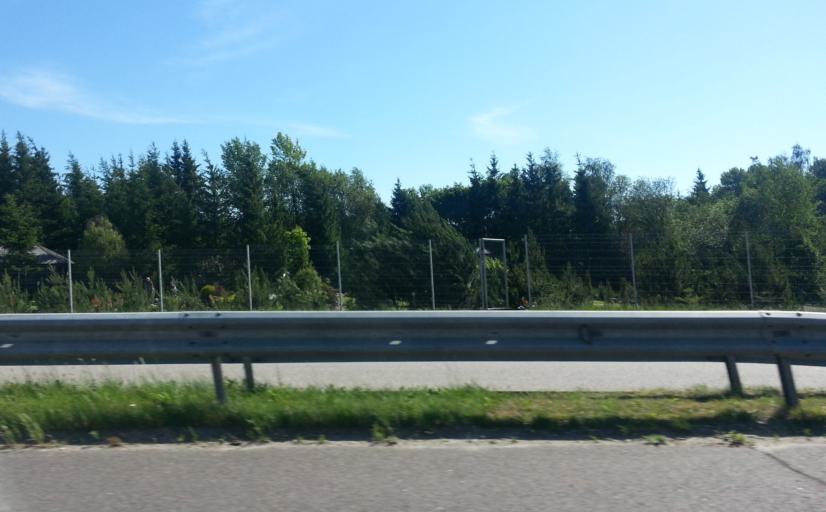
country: LT
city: Sirvintos
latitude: 55.0758
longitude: 24.8803
